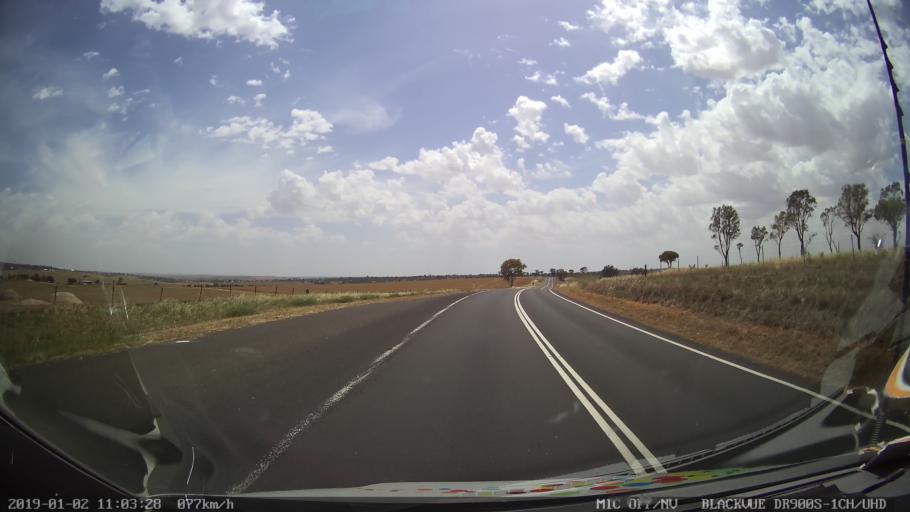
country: AU
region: New South Wales
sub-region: Young
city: Young
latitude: -34.5777
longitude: 148.3386
